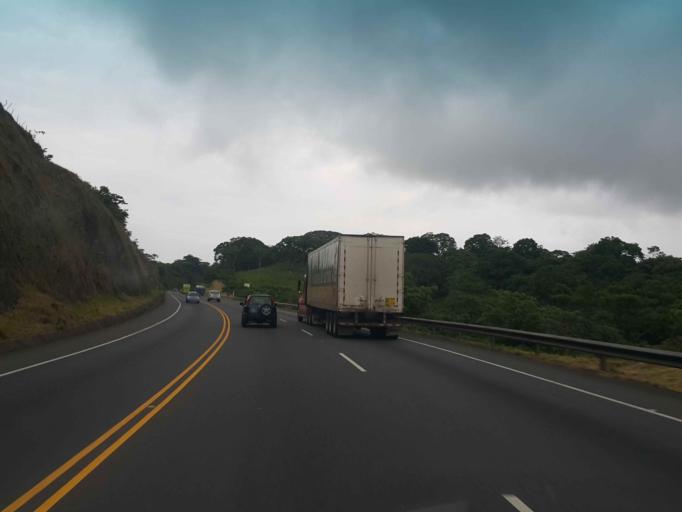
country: CR
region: Alajuela
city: Atenas
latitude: 9.9652
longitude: -84.3399
